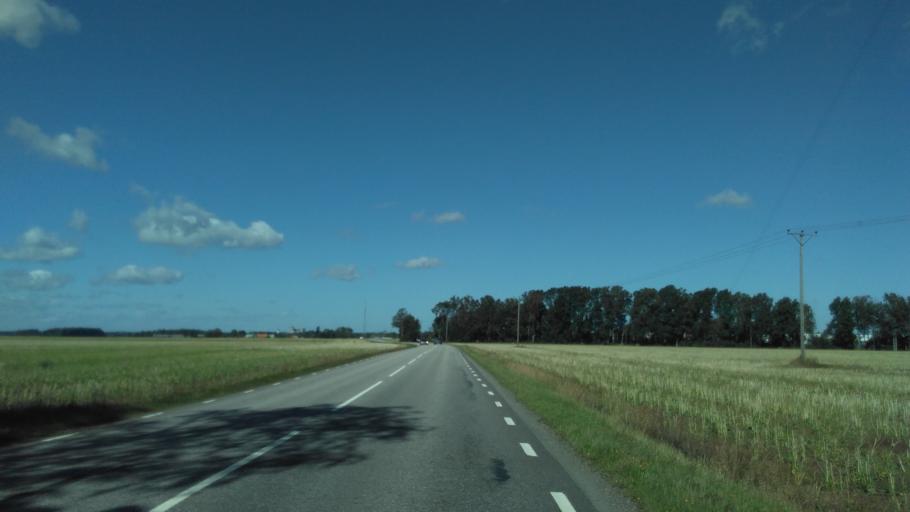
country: SE
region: Vaestra Goetaland
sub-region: Vara Kommun
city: Vara
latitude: 58.2358
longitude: 13.0006
